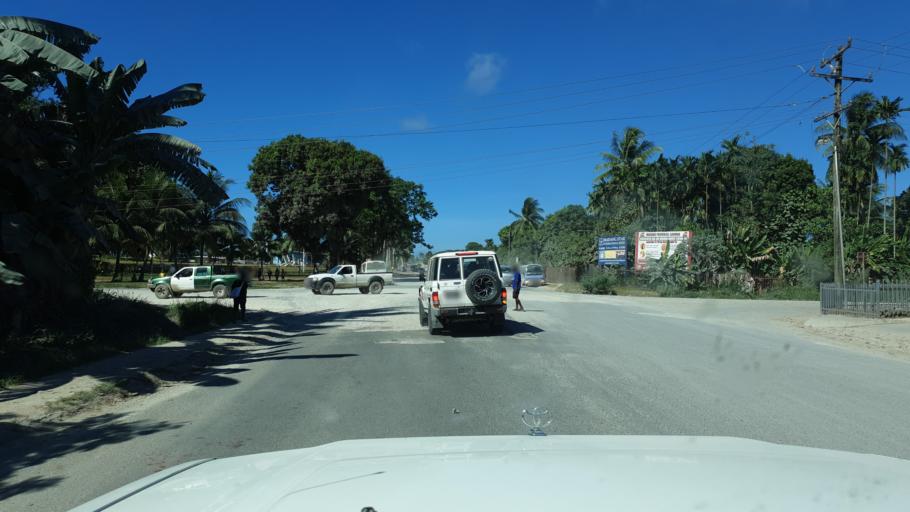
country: PG
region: Madang
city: Madang
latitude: -5.2364
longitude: 145.7876
